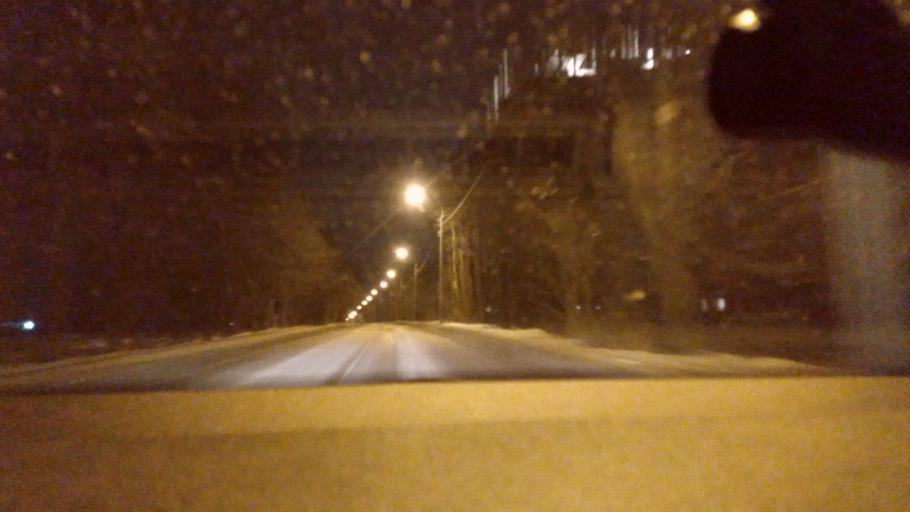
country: RU
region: Moskovskaya
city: Zheleznodorozhnyy
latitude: 55.7427
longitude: 38.0401
